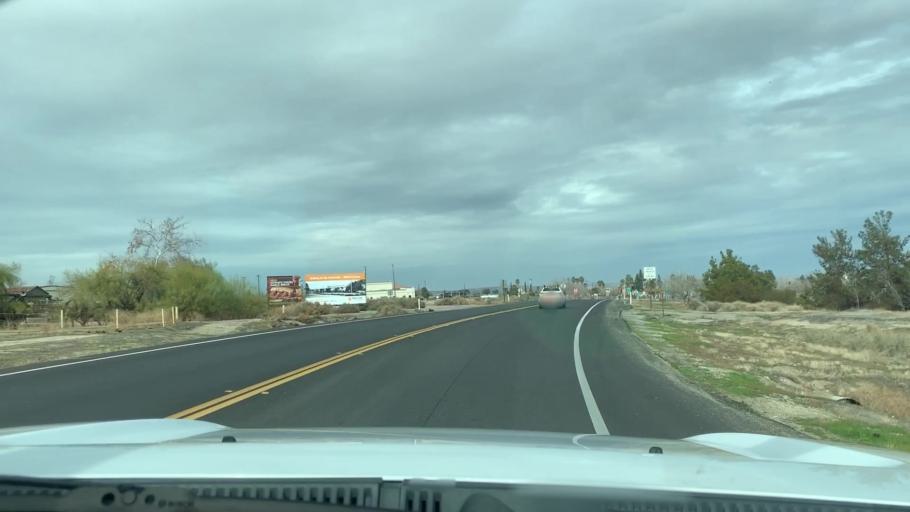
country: US
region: California
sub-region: Kern County
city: South Taft
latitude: 35.1332
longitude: -119.4469
